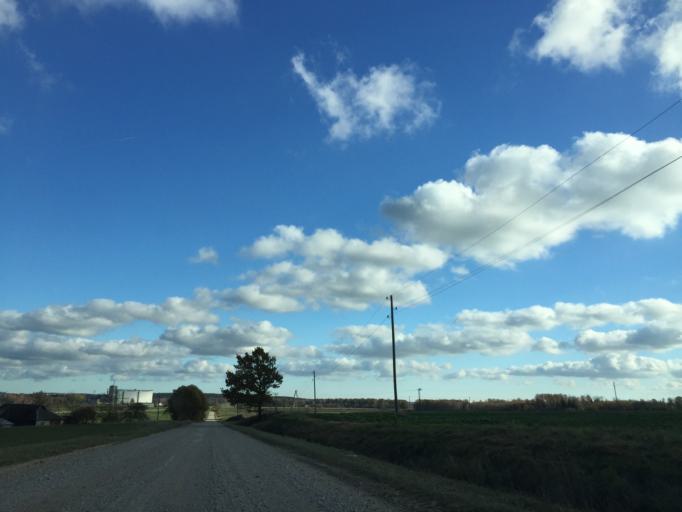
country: LV
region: Tukuma Rajons
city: Tukums
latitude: 56.9528
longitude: 23.0770
